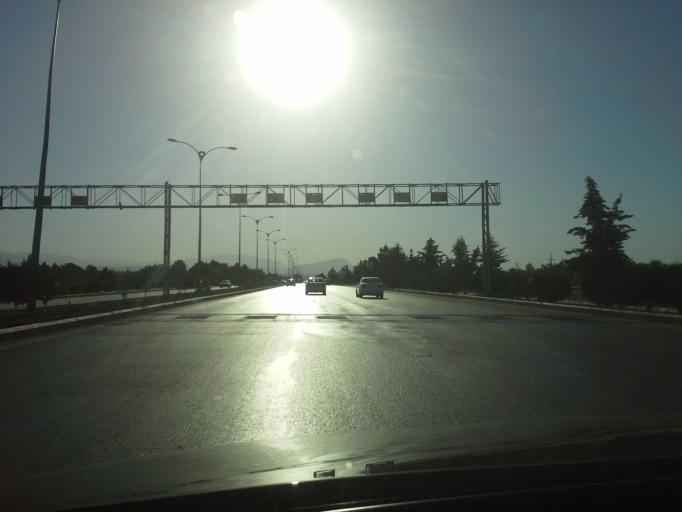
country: TM
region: Ahal
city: Annau
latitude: 37.9168
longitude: 58.4675
